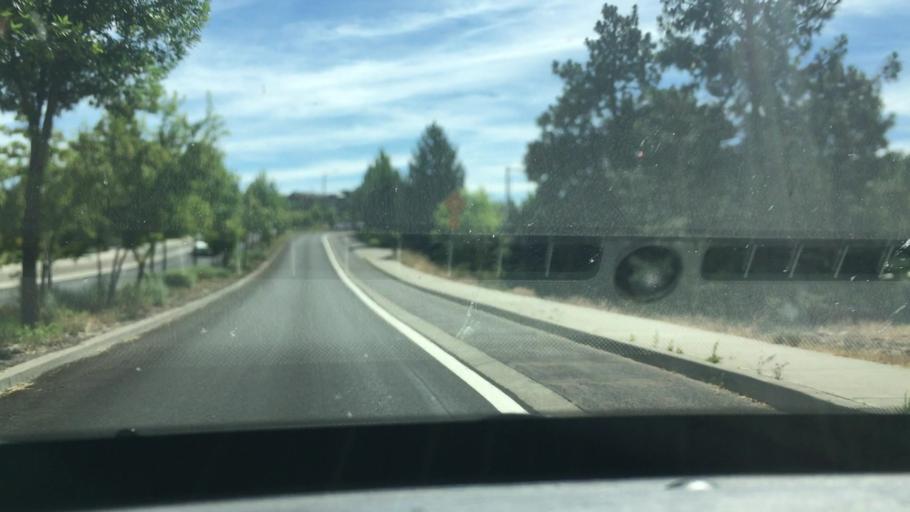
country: US
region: Oregon
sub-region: Deschutes County
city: Bend
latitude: 44.0407
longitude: -121.3194
